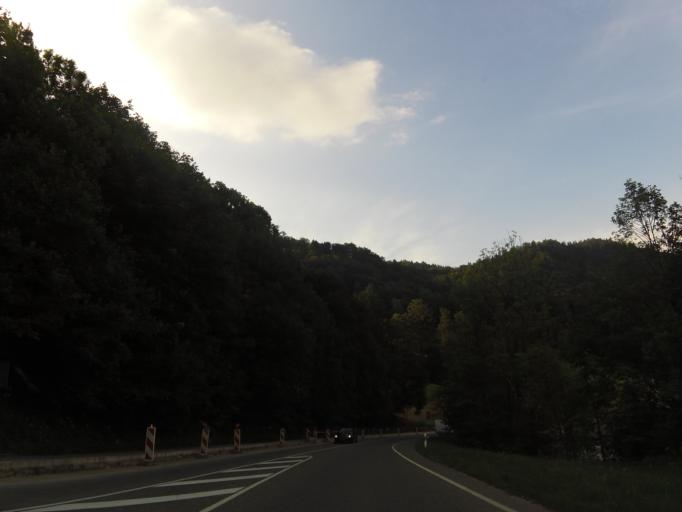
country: DE
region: Bavaria
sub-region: Upper Bavaria
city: Berchtesgaden
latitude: 47.6401
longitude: 13.0160
